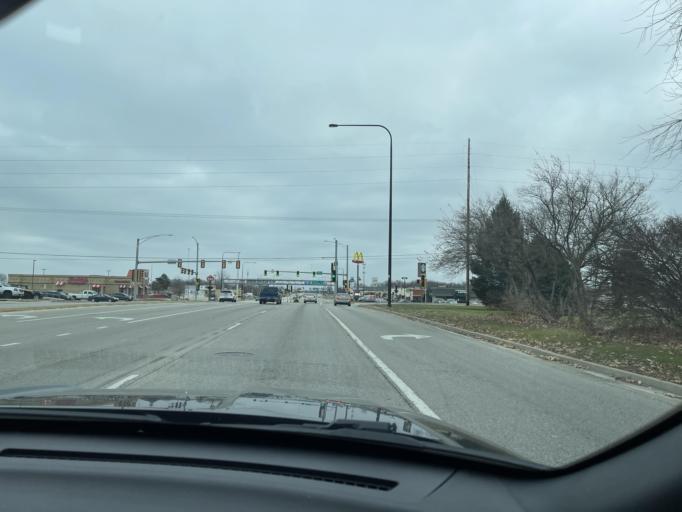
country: US
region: Illinois
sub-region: Sangamon County
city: Grandview
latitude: 39.8019
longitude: -89.6071
